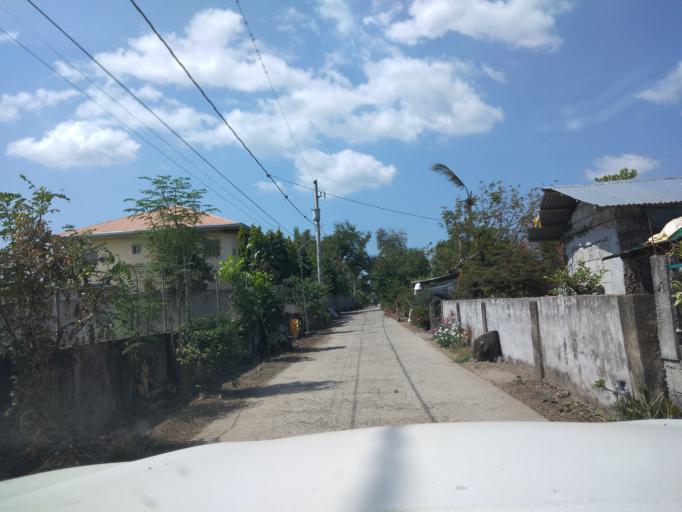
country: PH
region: Central Luzon
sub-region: Province of Pampanga
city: Bahay Pare
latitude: 15.0448
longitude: 120.8843
